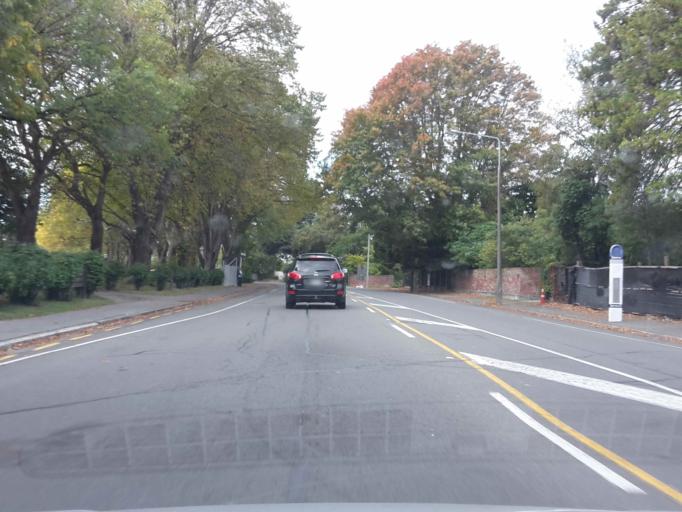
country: NZ
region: Canterbury
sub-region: Christchurch City
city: Christchurch
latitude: -43.5132
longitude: 172.6100
